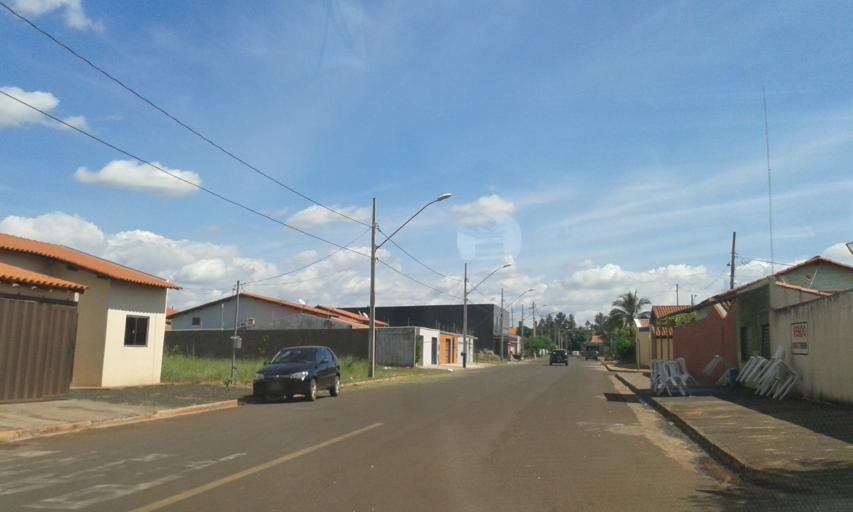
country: BR
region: Minas Gerais
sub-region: Santa Vitoria
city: Santa Vitoria
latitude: -18.8536
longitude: -50.1266
